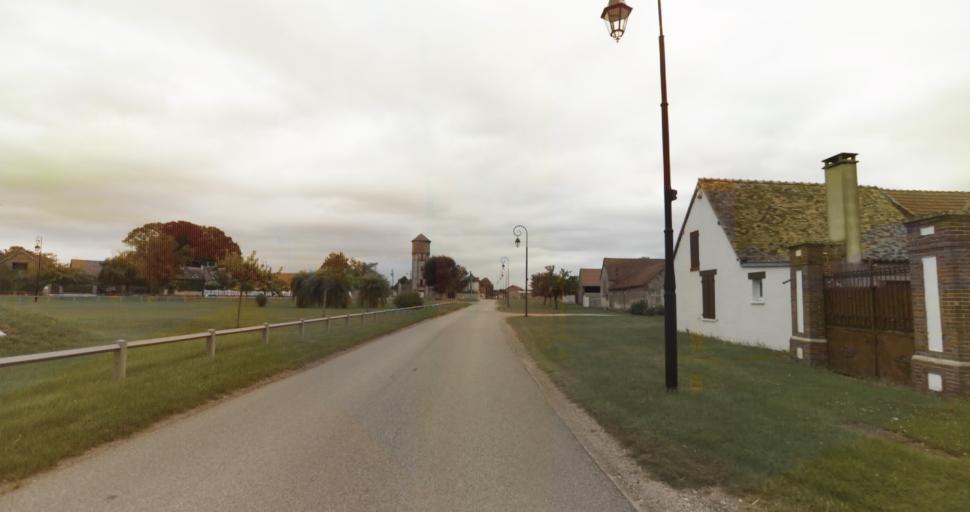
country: FR
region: Haute-Normandie
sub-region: Departement de l'Eure
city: La Couture-Boussey
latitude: 48.9344
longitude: 1.3967
